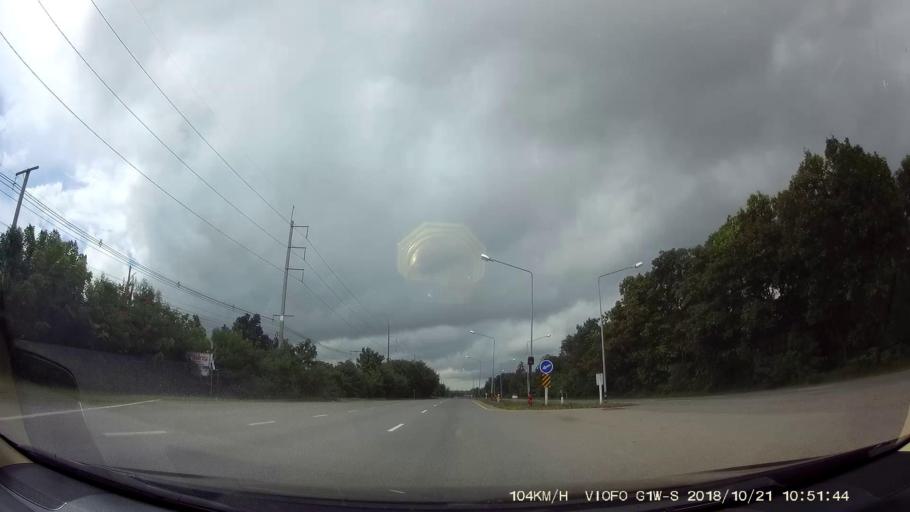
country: TH
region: Chaiyaphum
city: Khon Sawan
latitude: 15.9840
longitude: 102.2009
